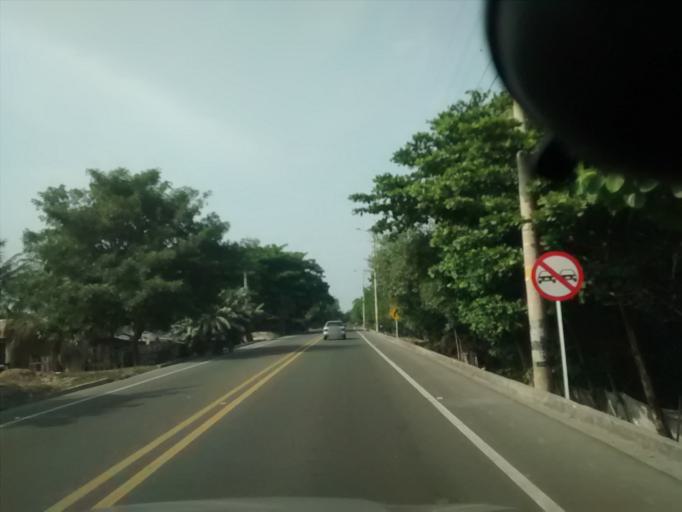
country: CO
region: Bolivar
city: Cartagena
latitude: 10.4733
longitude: -75.4946
